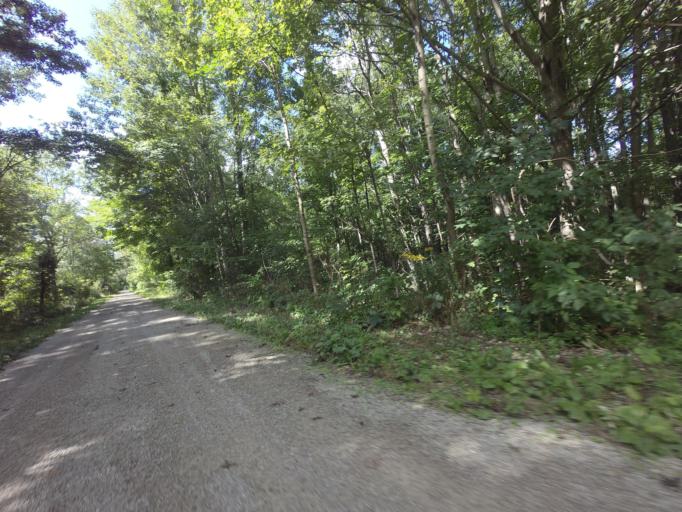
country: CA
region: Ontario
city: Huron East
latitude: 43.6754
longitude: -81.2878
